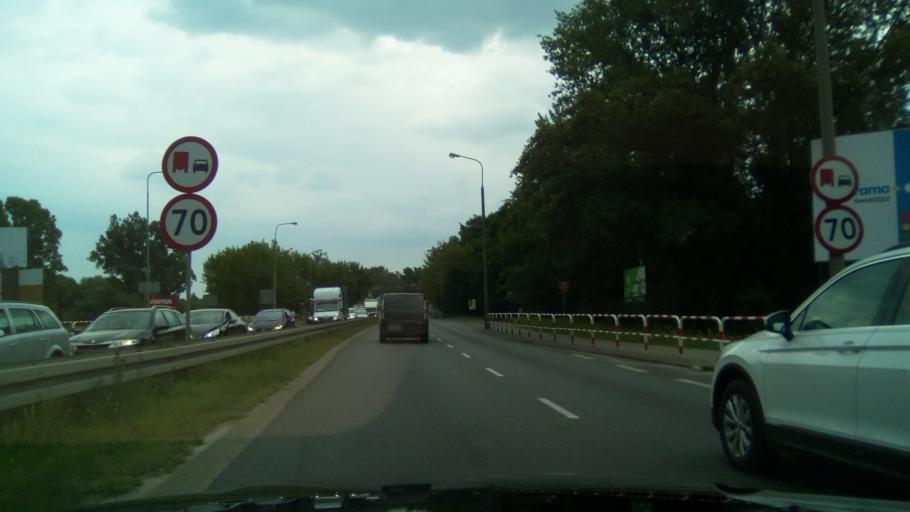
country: PL
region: Greater Poland Voivodeship
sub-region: Powiat poznanski
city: Swarzedz
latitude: 52.4043
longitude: 17.0568
